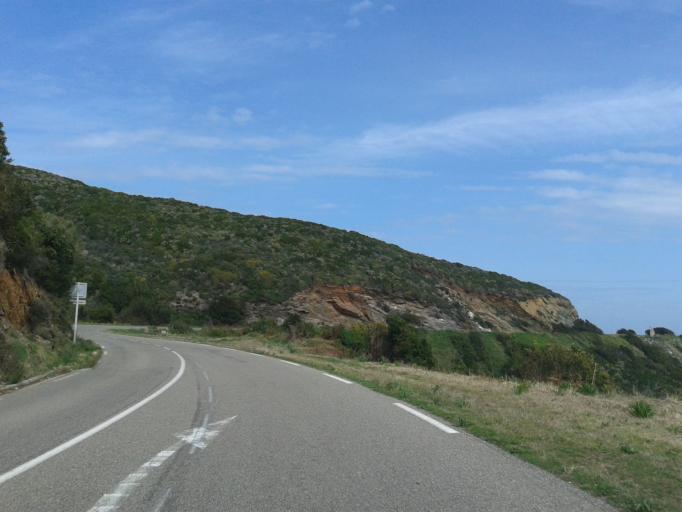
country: FR
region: Corsica
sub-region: Departement de la Haute-Corse
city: Brando
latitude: 42.8498
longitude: 9.4829
